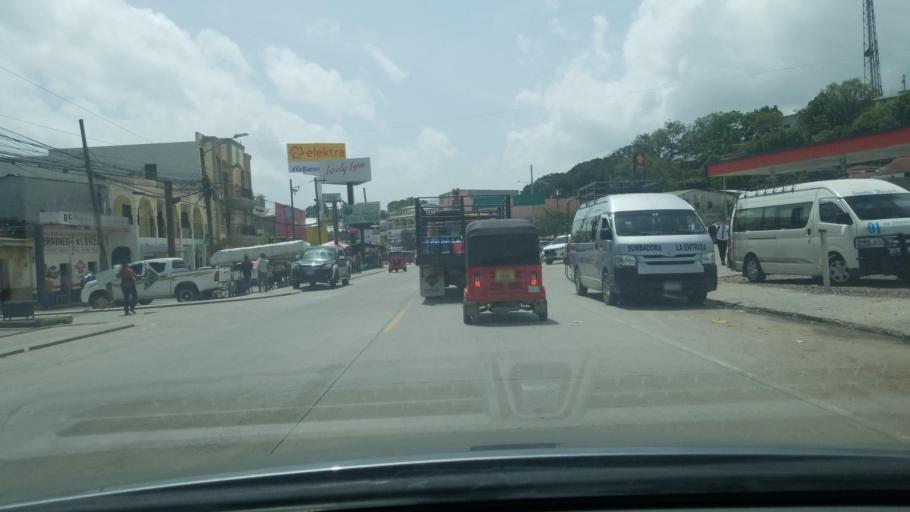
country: HN
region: Copan
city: La Entrada
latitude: 15.0601
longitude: -88.7540
